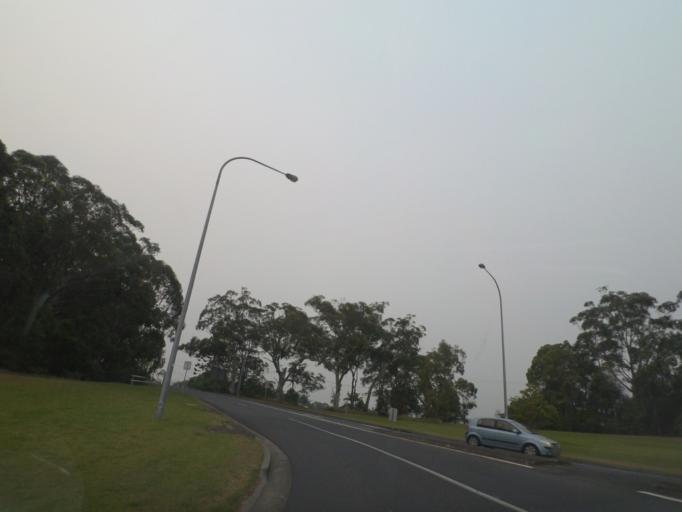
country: AU
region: New South Wales
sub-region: Coffs Harbour
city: Coffs Harbour
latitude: -30.3055
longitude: 153.1223
